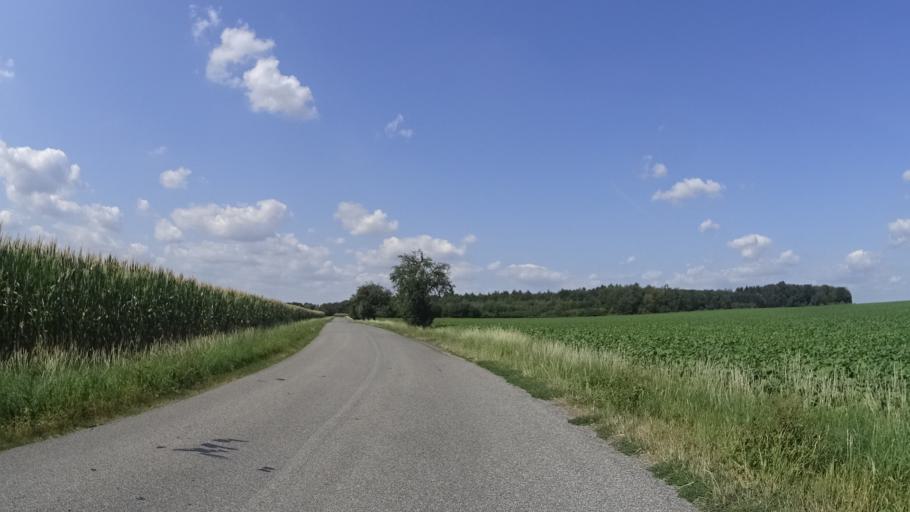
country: CZ
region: Kralovehradecky
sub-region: Okres Jicin
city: Jicin
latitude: 50.3690
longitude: 15.3637
